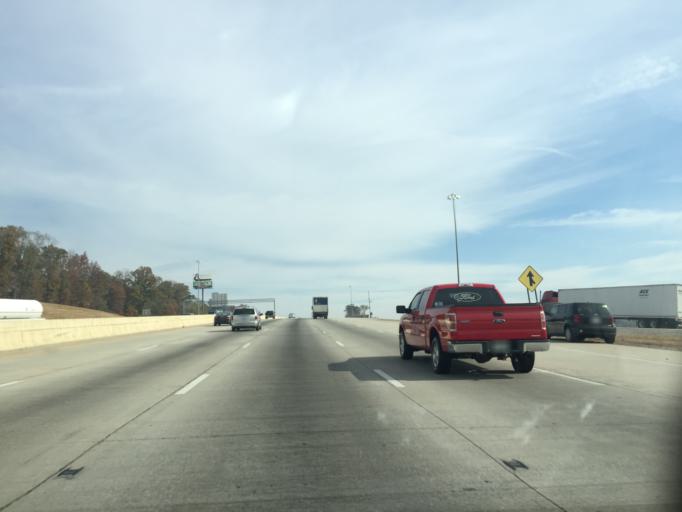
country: US
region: Tennessee
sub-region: Hamilton County
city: Harrison
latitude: 35.0746
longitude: -85.1087
